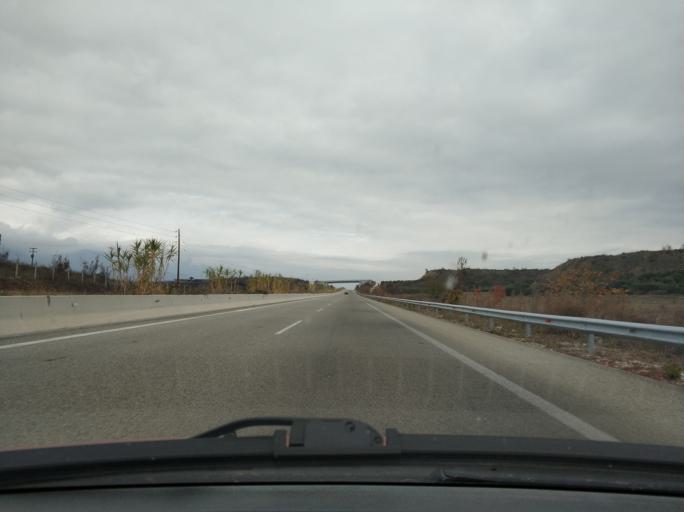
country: GR
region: East Macedonia and Thrace
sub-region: Nomos Kavalas
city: Paralia Ofryniou
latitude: 40.7967
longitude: 24.0116
